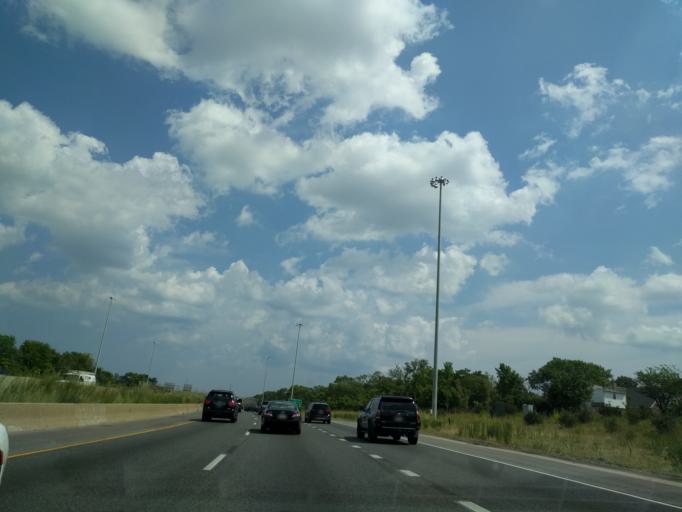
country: US
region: Illinois
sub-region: Cook County
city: Calumet Park
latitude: 41.7132
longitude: -87.6189
